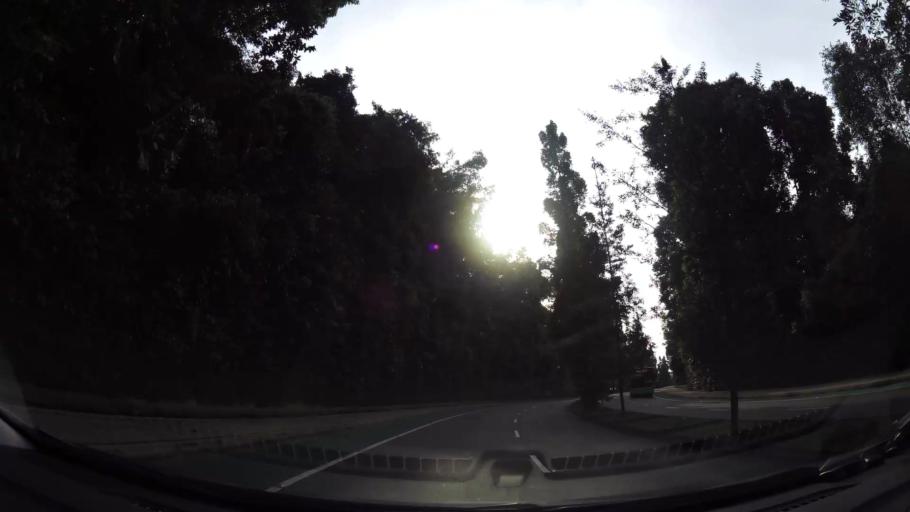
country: SG
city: Singapore
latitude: 1.2477
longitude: 103.8332
